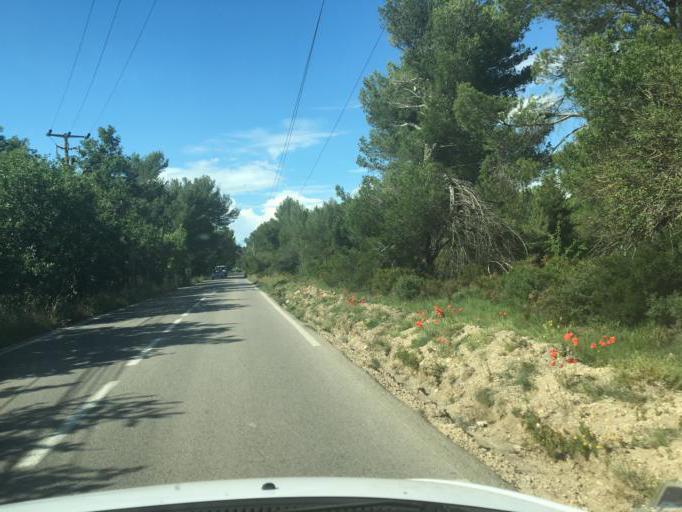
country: FR
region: Provence-Alpes-Cote d'Azur
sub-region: Departement des Bouches-du-Rhone
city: Eguilles
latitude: 43.5232
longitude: 5.3517
